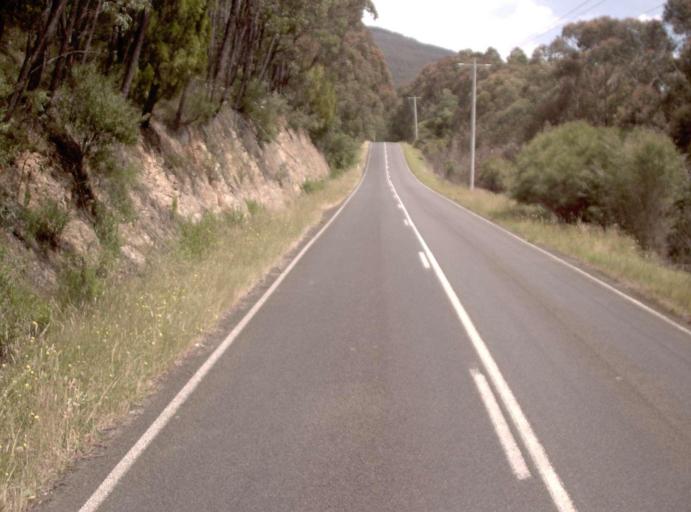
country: AU
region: Victoria
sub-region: Latrobe
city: Moe
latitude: -37.9051
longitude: 146.3928
